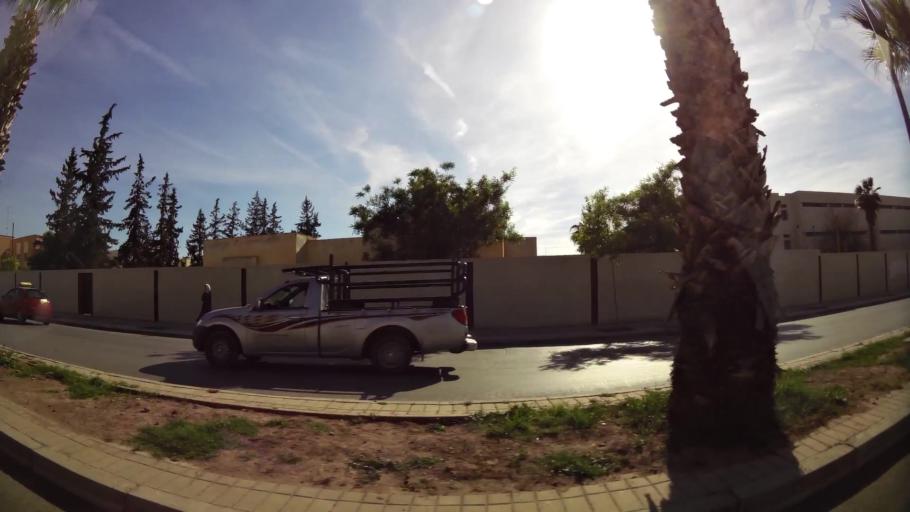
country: MA
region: Oriental
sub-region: Oujda-Angad
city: Oujda
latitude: 34.6649
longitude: -1.8959
